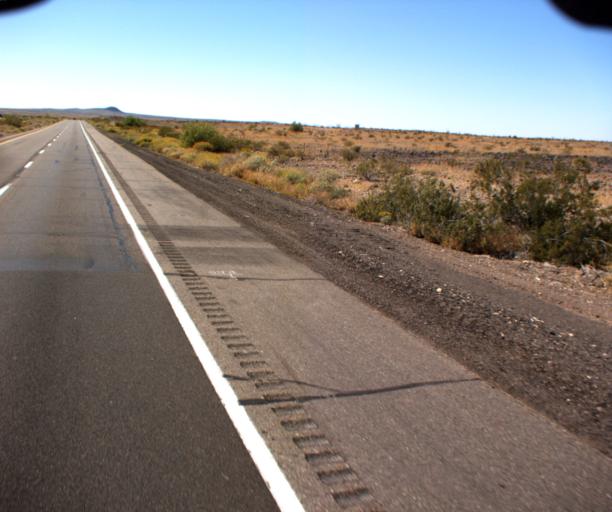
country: US
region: Arizona
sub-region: Maricopa County
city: Gila Bend
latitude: 32.8906
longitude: -113.0627
